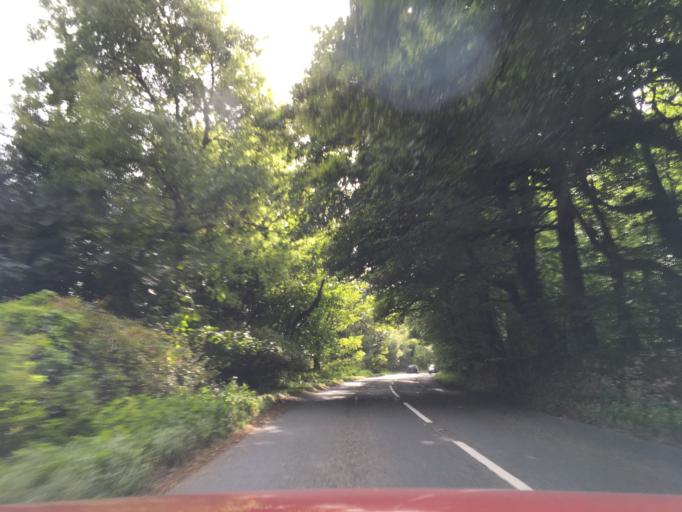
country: GB
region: England
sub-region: Gloucestershire
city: Wotton-under-Edge
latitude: 51.6619
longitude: -2.3166
